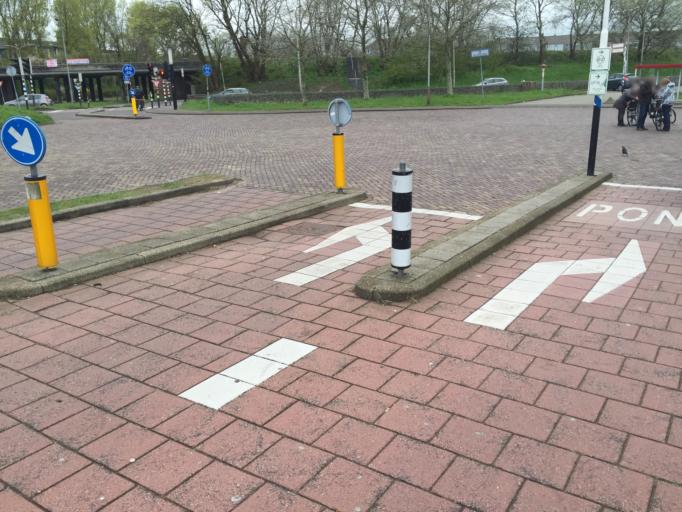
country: NL
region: North Holland
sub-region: Gemeente Velsen
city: Velsen-Zuid
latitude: 52.4625
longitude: 4.6325
